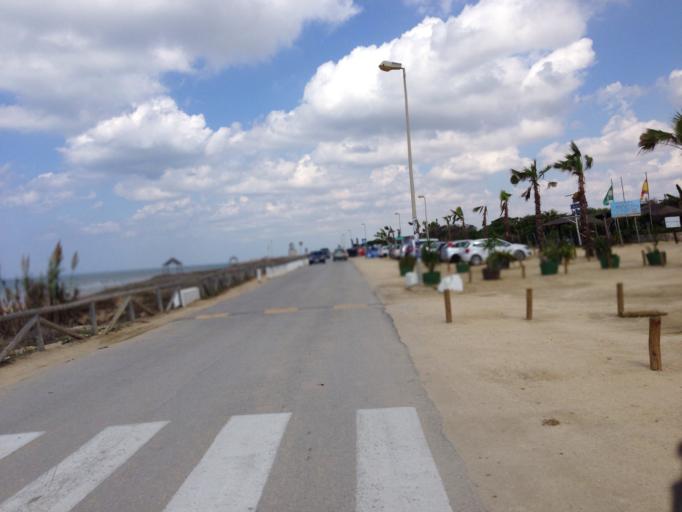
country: ES
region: Andalusia
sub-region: Provincia de Cadiz
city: Conil de la Frontera
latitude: 36.2268
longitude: -6.0666
